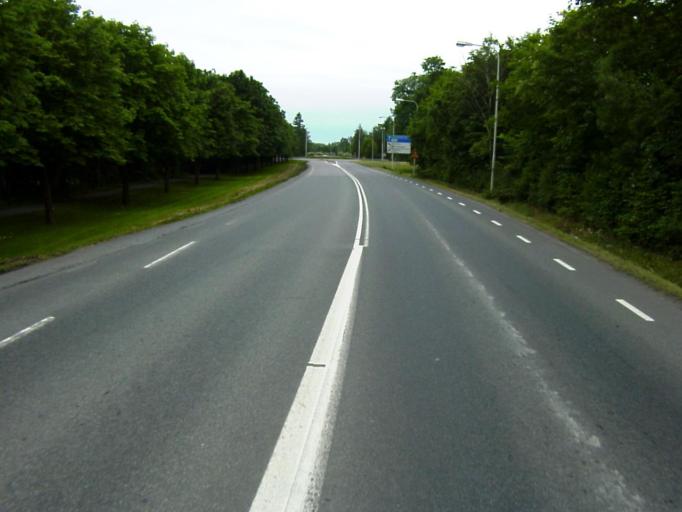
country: SE
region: Skane
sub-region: Kristianstads Kommun
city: Kristianstad
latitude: 56.0439
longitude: 14.1542
